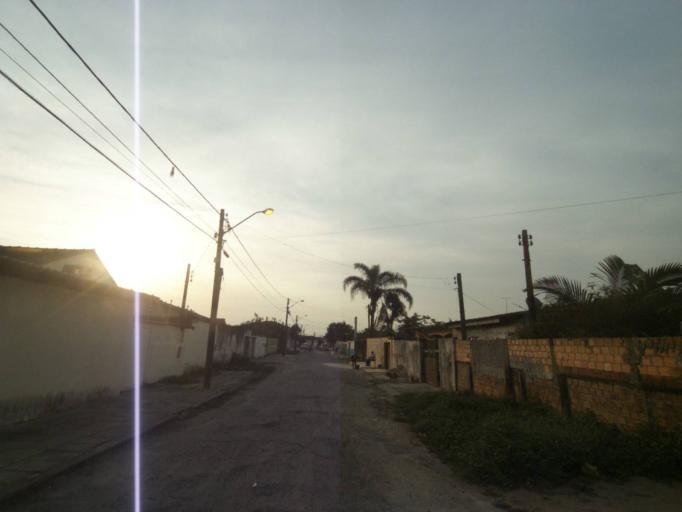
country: BR
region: Parana
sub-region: Paranagua
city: Paranagua
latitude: -25.5206
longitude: -48.5399
